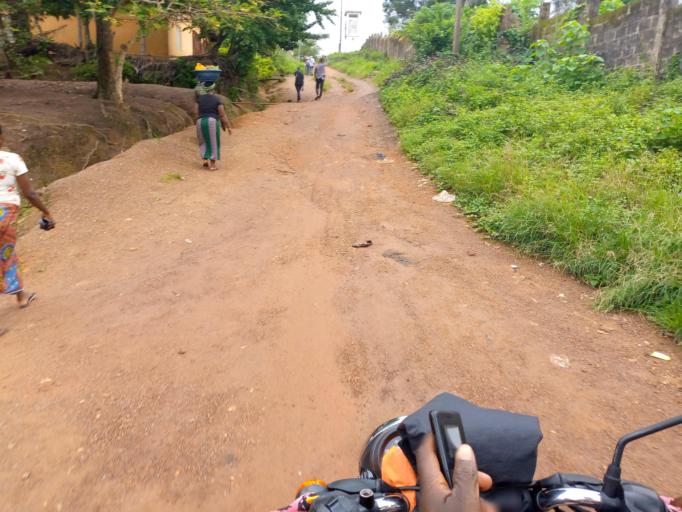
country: SL
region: Eastern Province
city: Kenema
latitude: 7.8733
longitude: -11.1848
